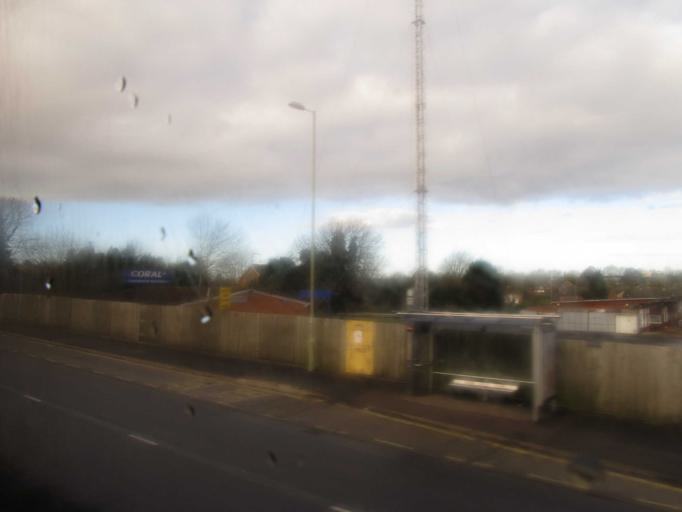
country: GB
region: England
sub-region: Hampshire
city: Basingstoke
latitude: 51.2514
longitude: -1.1106
